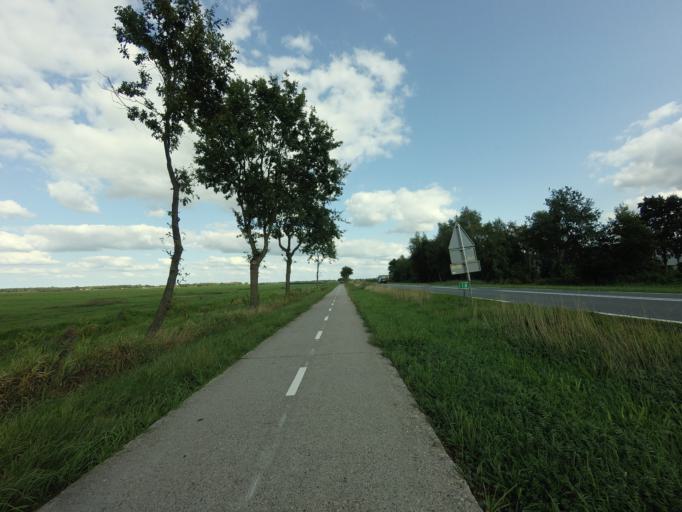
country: NL
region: Drenthe
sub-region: Gemeente Westerveld
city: Dwingeloo
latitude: 52.8394
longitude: 6.3778
